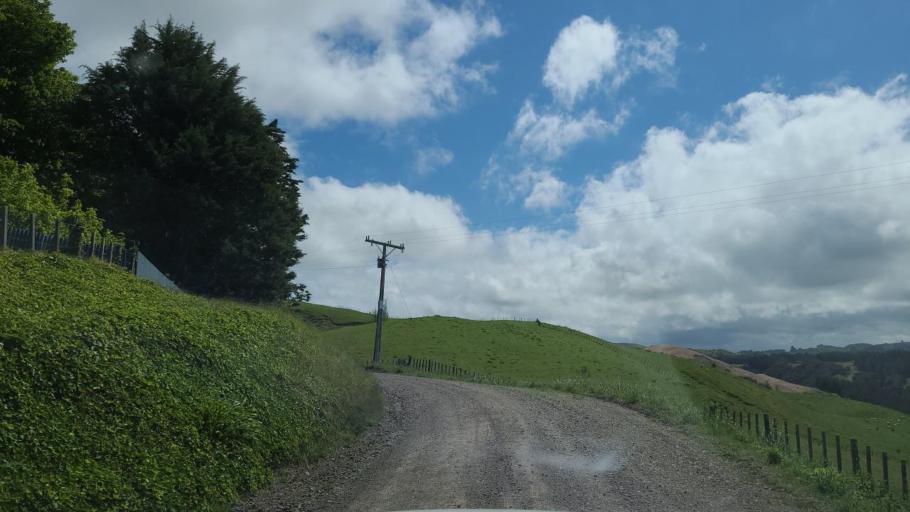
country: NZ
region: Hawke's Bay
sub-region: Napier City
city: Napier
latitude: -39.3680
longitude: 176.7951
